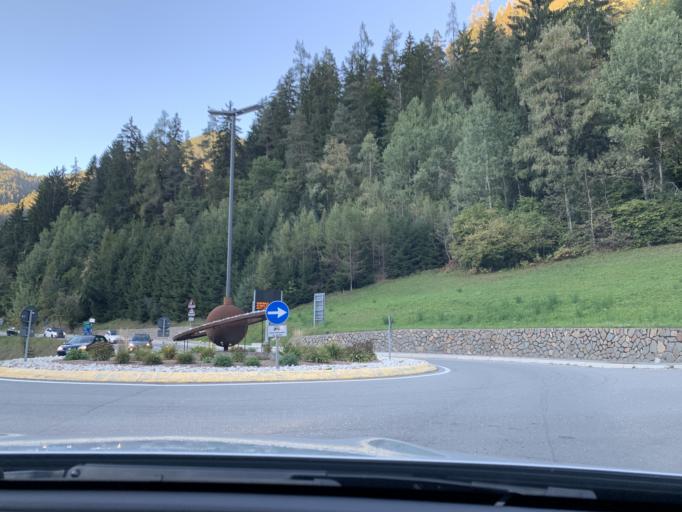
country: IT
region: Trentino-Alto Adige
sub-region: Bolzano
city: Nova Ponente
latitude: 46.4370
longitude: 11.4676
